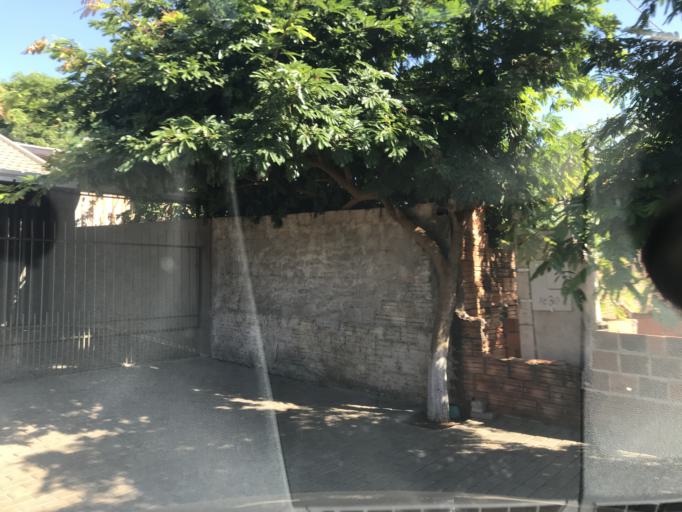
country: BR
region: Parana
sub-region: Palotina
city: Palotina
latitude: -24.2804
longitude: -53.8243
